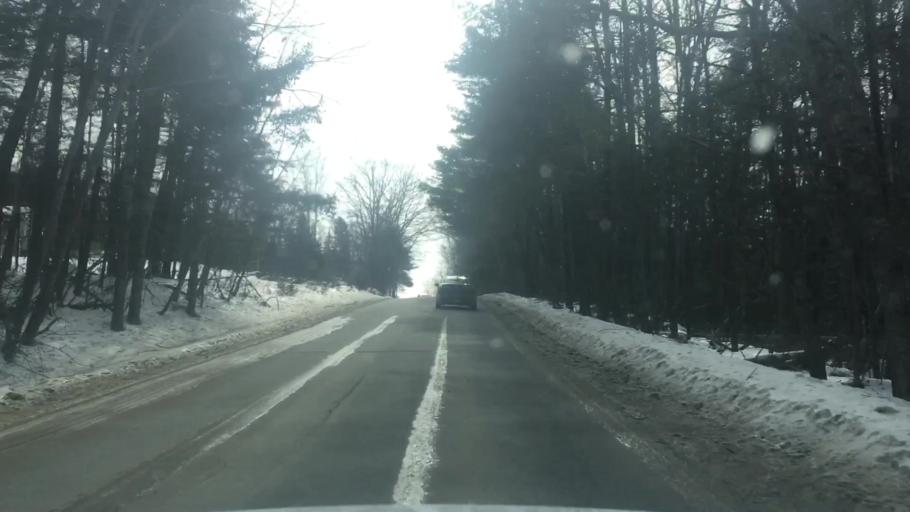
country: US
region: Maine
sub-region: Hancock County
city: Orland
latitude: 44.5896
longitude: -68.7255
